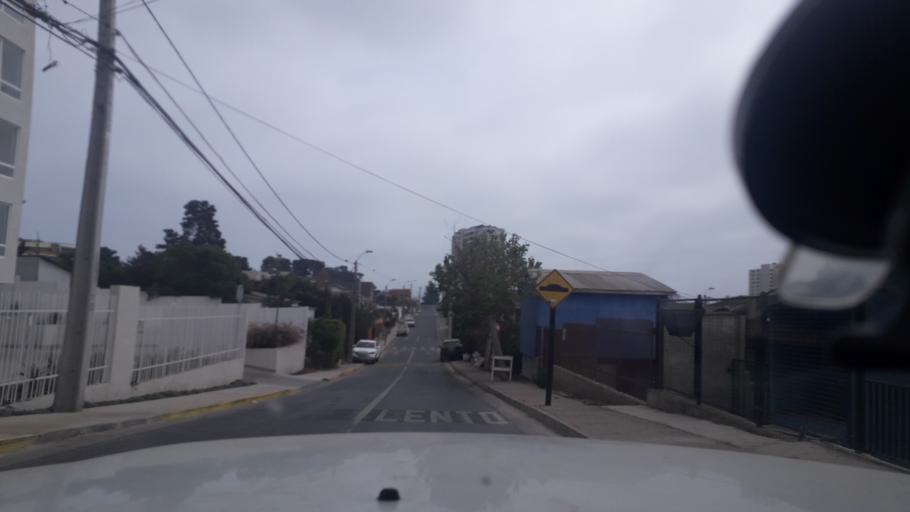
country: CL
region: Valparaiso
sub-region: Provincia de Valparaiso
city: Vina del Mar
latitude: -32.9380
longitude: -71.5296
